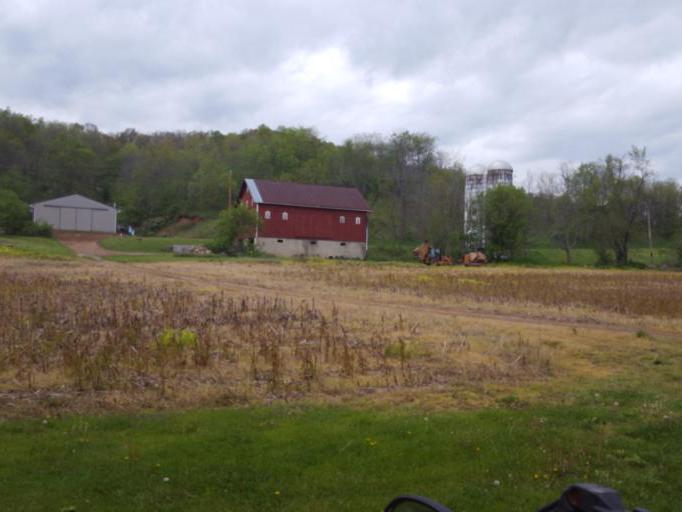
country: US
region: Ohio
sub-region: Ashland County
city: Loudonville
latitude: 40.5441
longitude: -82.2058
